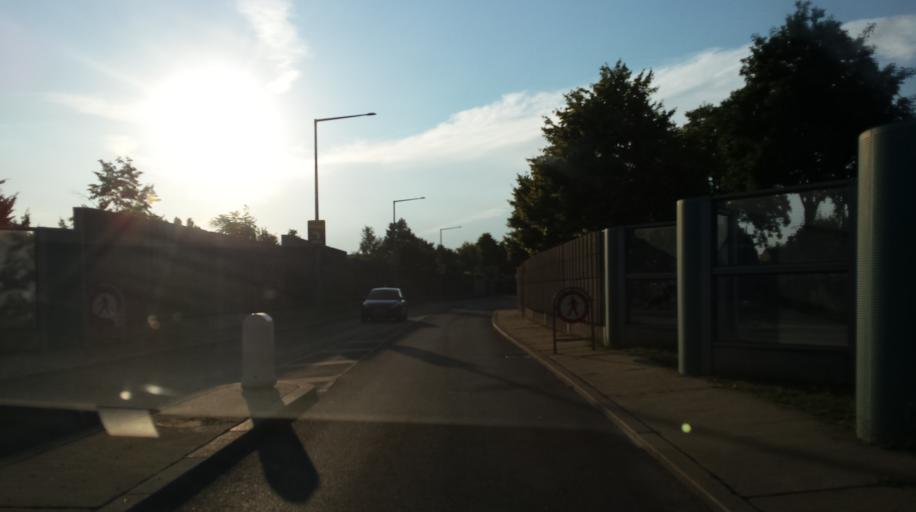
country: AT
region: Lower Austria
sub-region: Politischer Bezirk Wien-Umgebung
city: Gerasdorf bei Wien
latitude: 48.2584
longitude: 16.4156
